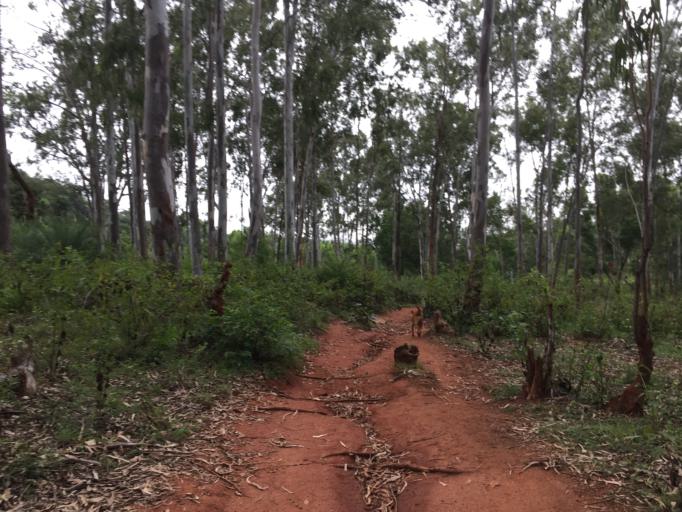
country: IN
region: Karnataka
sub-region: Bangalore Urban
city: Bangalore
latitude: 12.8838
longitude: 77.5291
